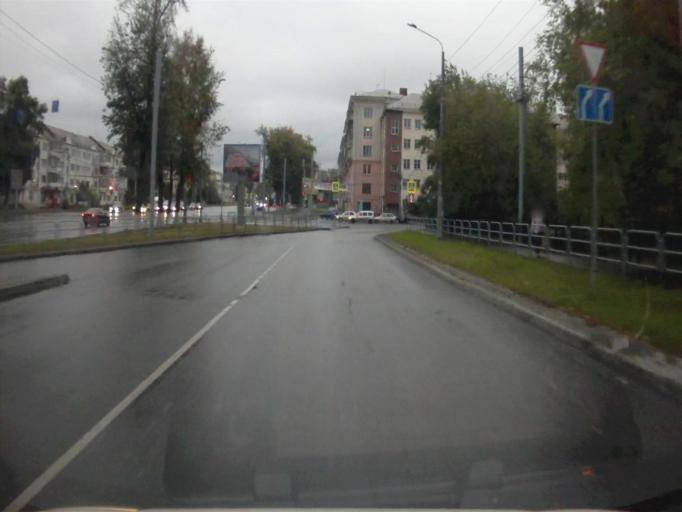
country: RU
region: Chelyabinsk
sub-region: Gorod Chelyabinsk
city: Chelyabinsk
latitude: 55.1603
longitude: 61.4439
